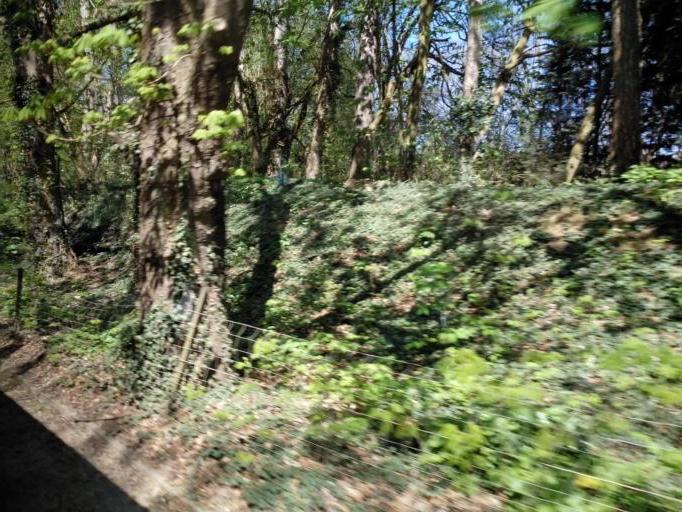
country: BE
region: Flanders
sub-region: Provincie Vlaams-Brabant
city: Bertem
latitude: 50.8510
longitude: 4.5917
